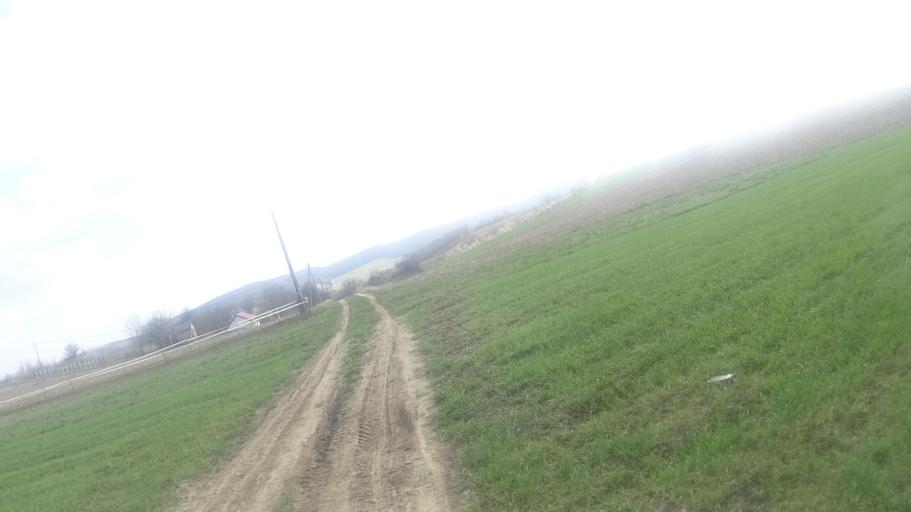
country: HU
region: Somogy
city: Adand
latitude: 46.8117
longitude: 18.1011
